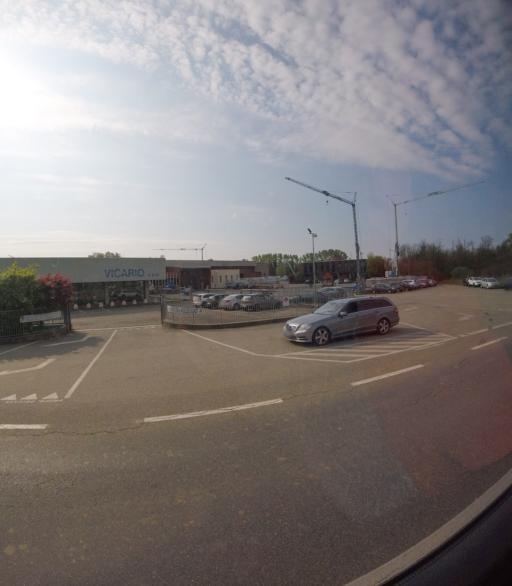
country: IT
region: Piedmont
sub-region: Provincia di Novara
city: Borgomanero
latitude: 45.7144
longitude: 8.4832
